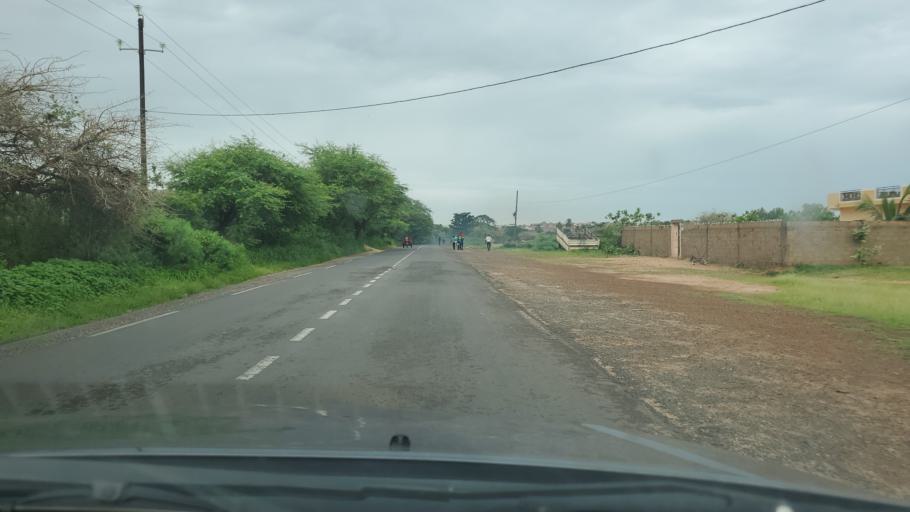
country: SN
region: Thies
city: Mekhe
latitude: 15.1276
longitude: -16.8632
